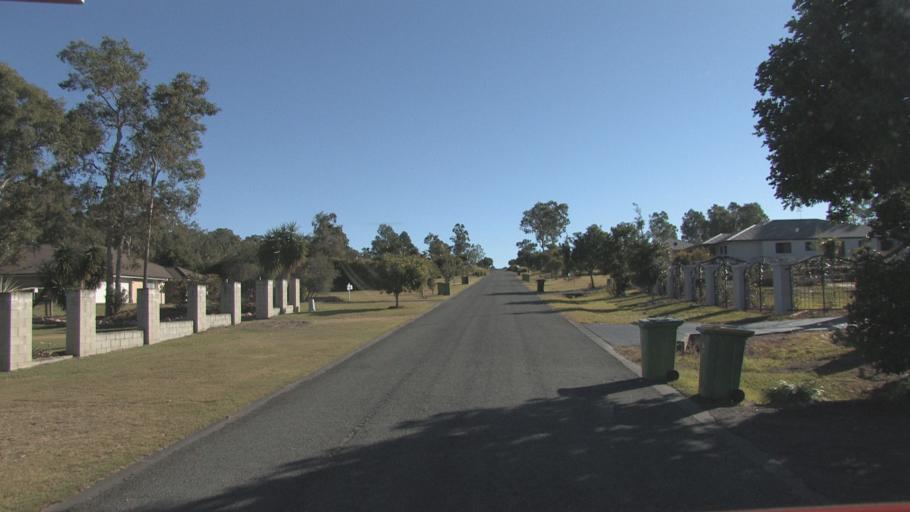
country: AU
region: Queensland
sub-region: Logan
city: North Maclean
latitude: -27.7500
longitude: 152.9590
